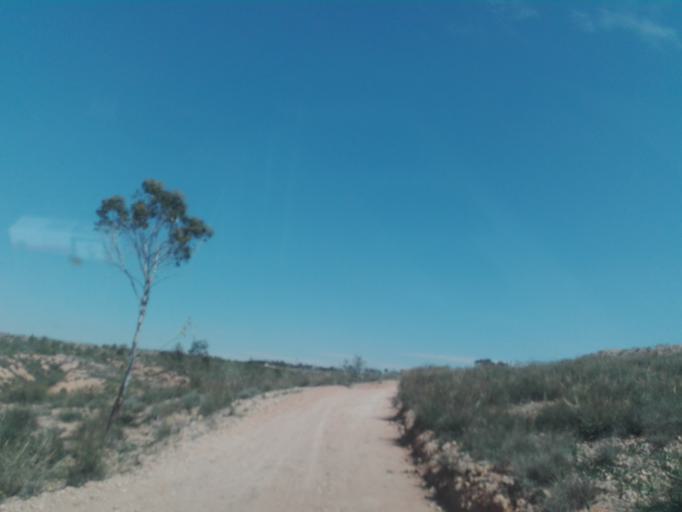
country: TN
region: Safaqis
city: Sfax
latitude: 34.6970
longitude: 10.5302
